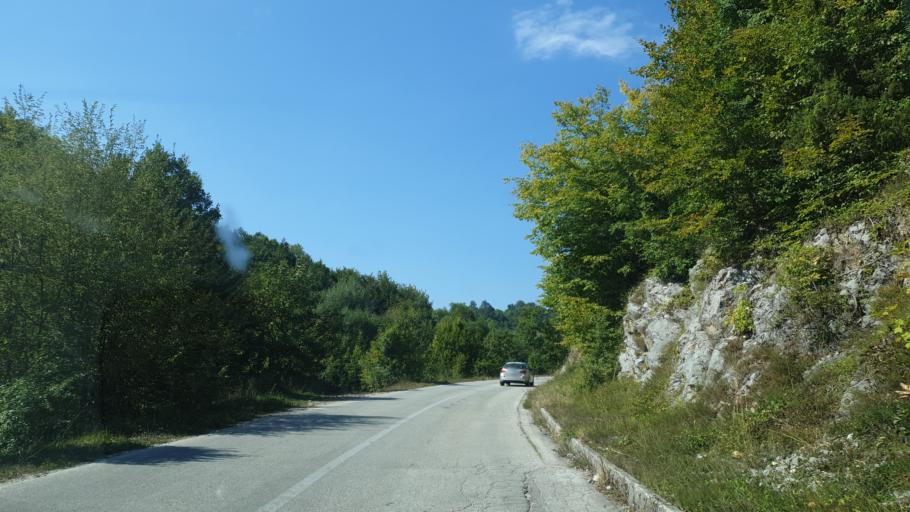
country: RS
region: Central Serbia
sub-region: Zlatiborski Okrug
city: Cajetina
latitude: 43.7113
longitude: 19.8369
